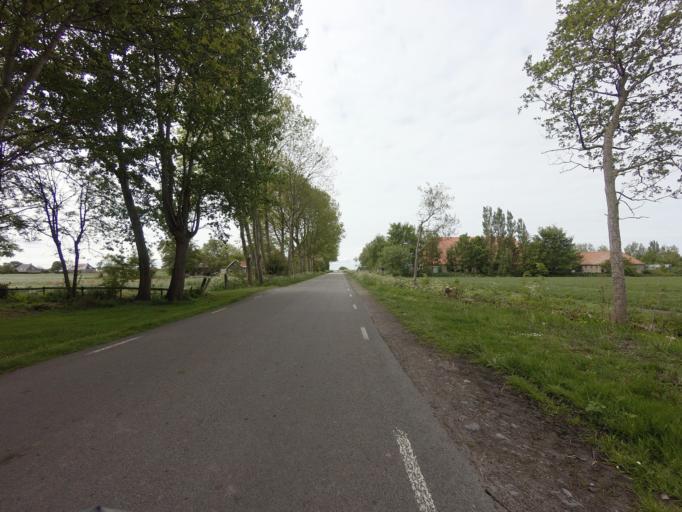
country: NL
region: Friesland
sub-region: Sudwest Fryslan
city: Koudum
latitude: 52.9446
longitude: 5.4894
